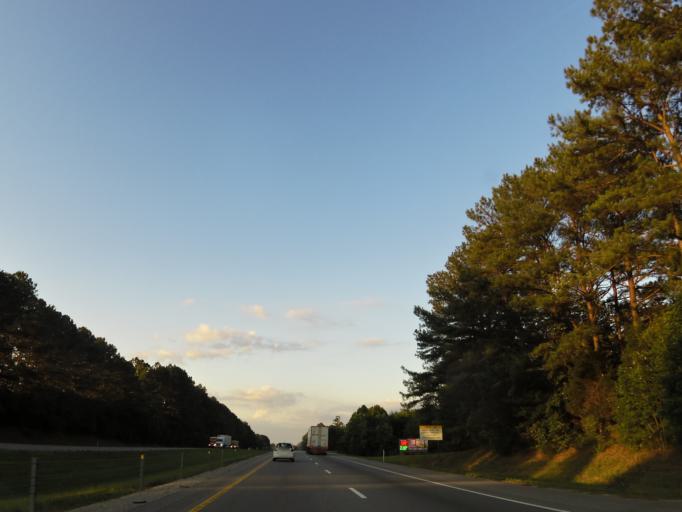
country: US
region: Tennessee
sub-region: Putnam County
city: Baxter
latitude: 36.1052
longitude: -85.6982
